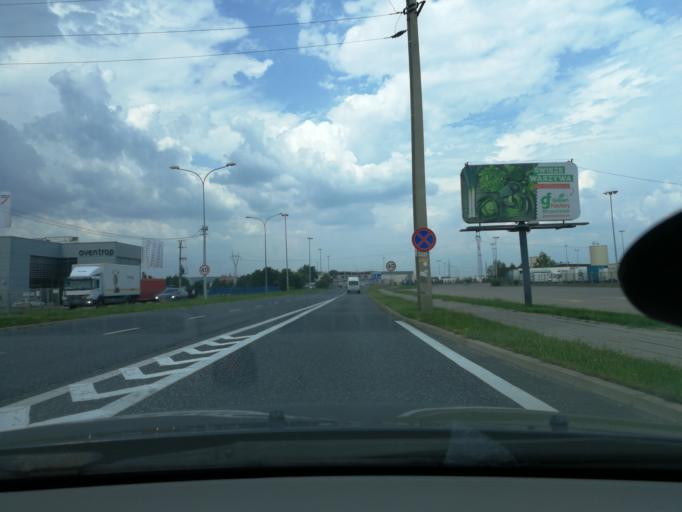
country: PL
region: Masovian Voivodeship
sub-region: Powiat pruszkowski
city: Piastow
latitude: 52.2161
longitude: 20.8393
